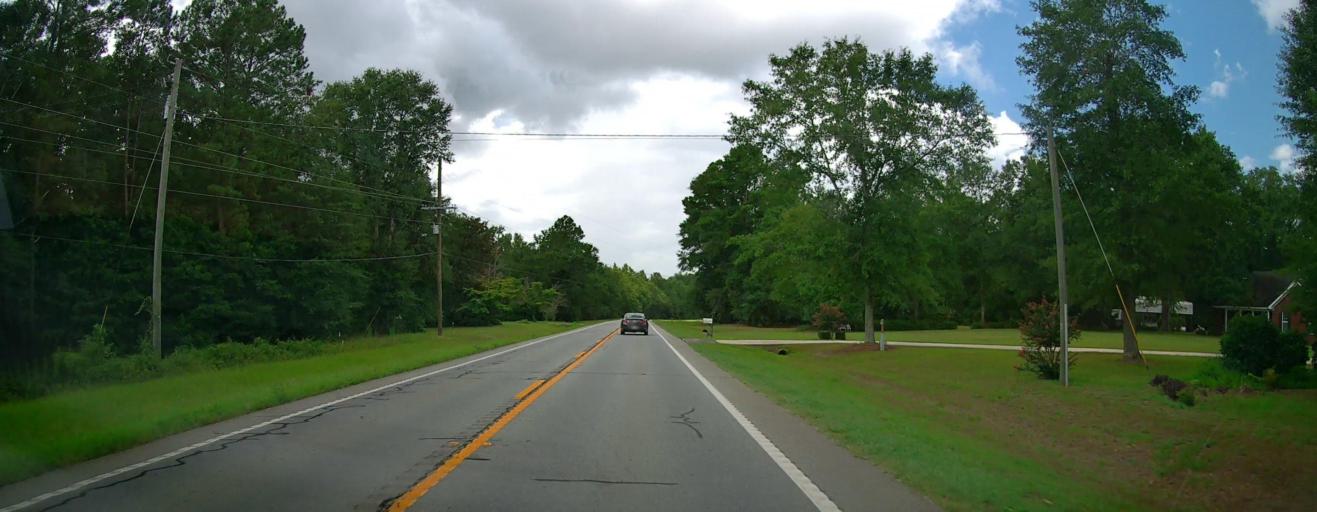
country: US
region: Georgia
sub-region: Pulaski County
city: Hawkinsville
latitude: 32.2443
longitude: -83.4984
